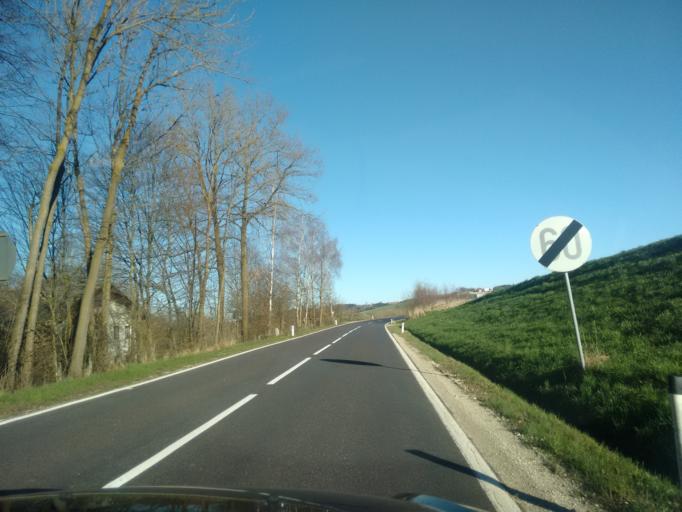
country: AT
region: Upper Austria
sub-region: Wels-Land
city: Offenhausen
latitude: 48.1782
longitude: 13.8263
